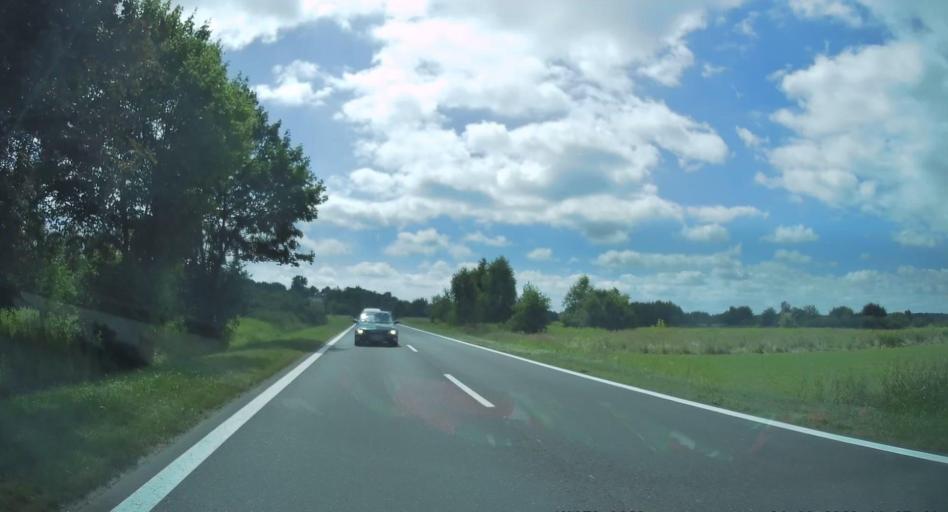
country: PL
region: Subcarpathian Voivodeship
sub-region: Powiat tarnobrzeski
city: Baranow Sandomierski
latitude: 50.4938
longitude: 21.5699
